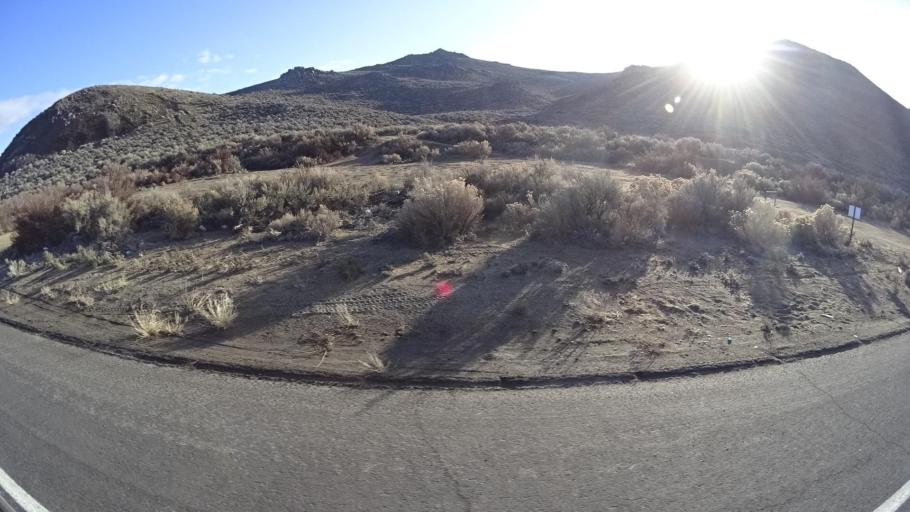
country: US
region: Nevada
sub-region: Washoe County
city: Cold Springs
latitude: 39.6613
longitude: -119.9602
